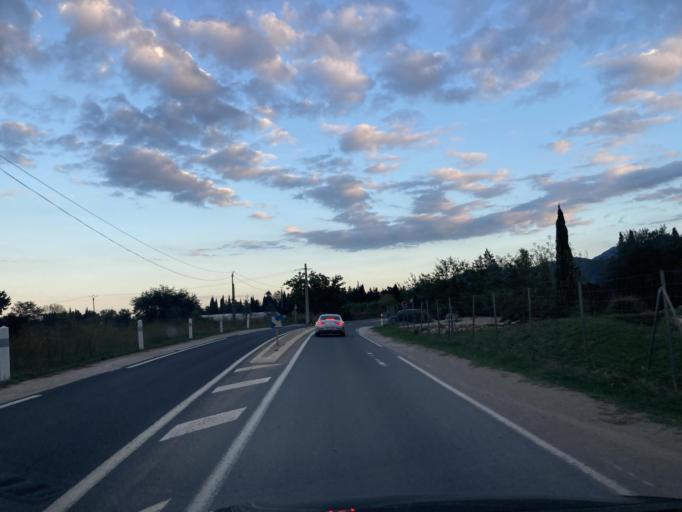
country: FR
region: Languedoc-Roussillon
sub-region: Departement des Pyrenees-Orientales
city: Sant Genis de Fontanes
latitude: 42.5578
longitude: 2.9086
